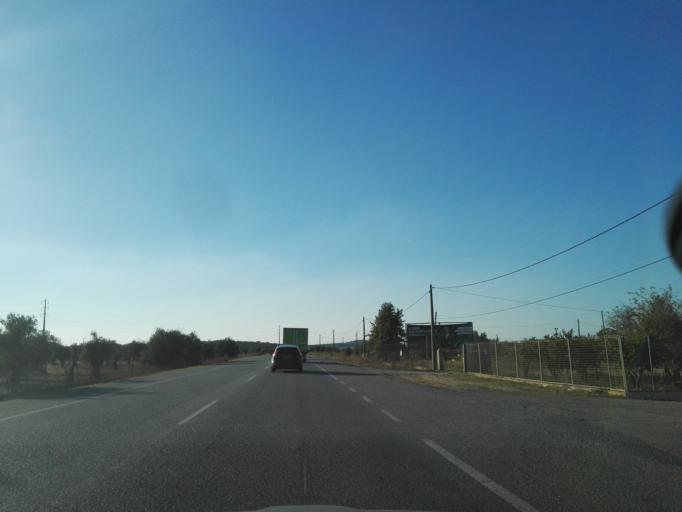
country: PT
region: Evora
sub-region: Borba
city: Borba
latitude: 38.8202
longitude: -7.4920
